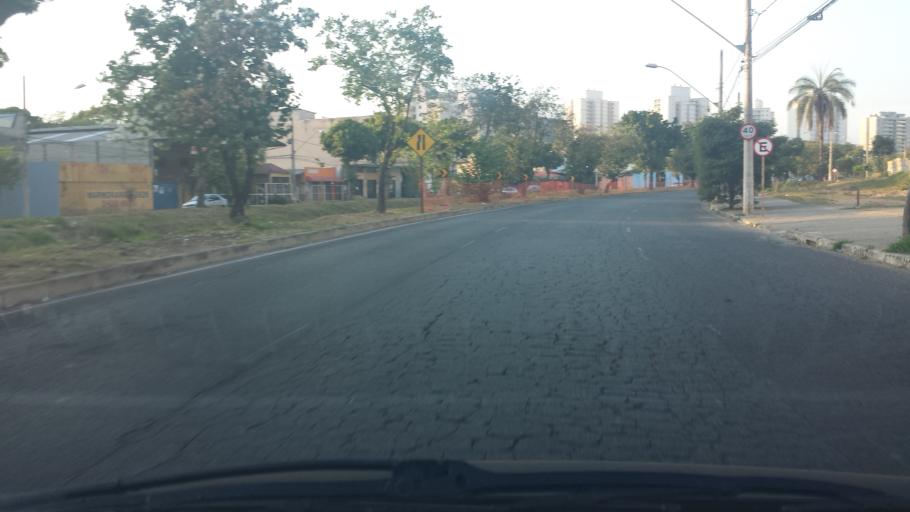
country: BR
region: Minas Gerais
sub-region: Belo Horizonte
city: Belo Horizonte
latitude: -19.8753
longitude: -43.9927
